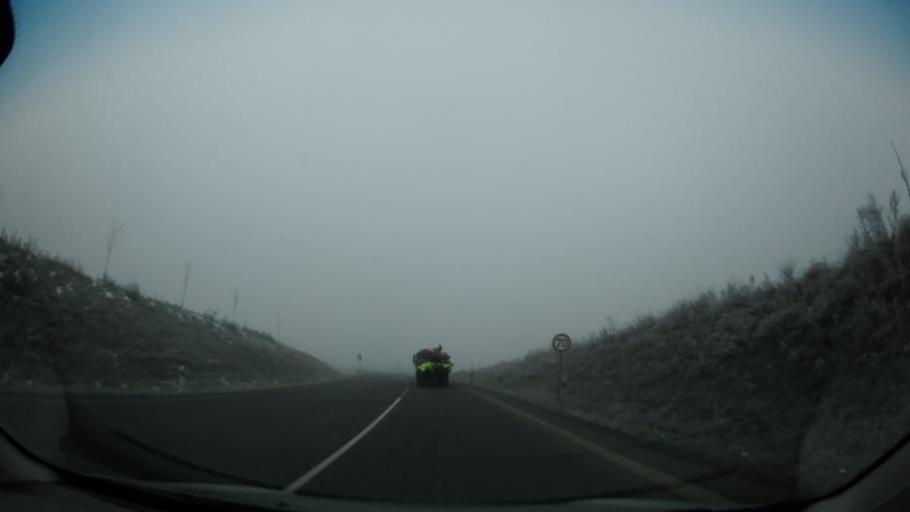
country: CZ
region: Vysocina
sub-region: Okres Trebic
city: Trebic
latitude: 49.2303
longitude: 15.8959
